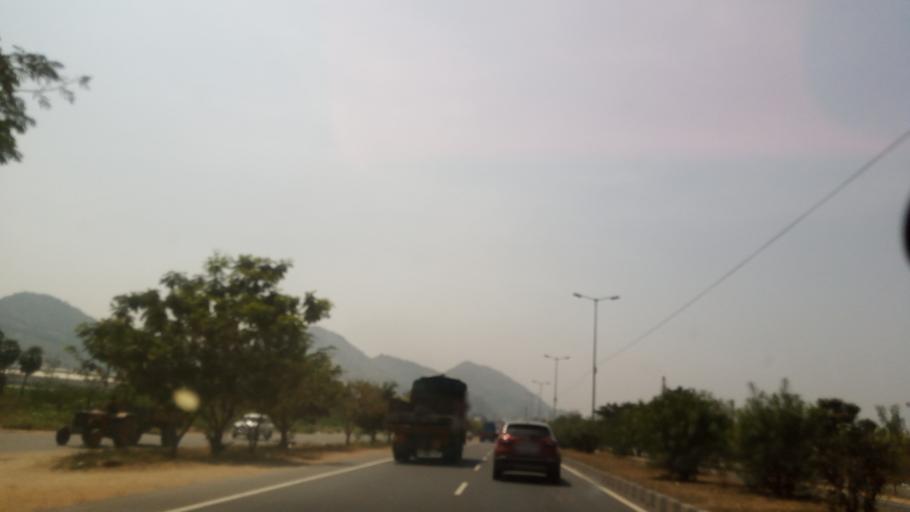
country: IN
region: Tamil Nadu
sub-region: Salem
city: Salem
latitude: 11.6393
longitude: 78.1732
